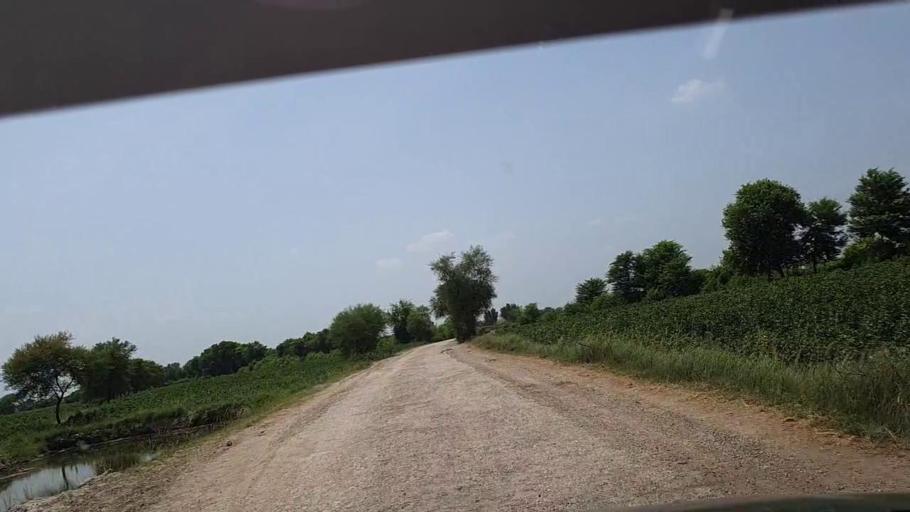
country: PK
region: Sindh
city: Khanpur
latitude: 27.8373
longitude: 69.4037
